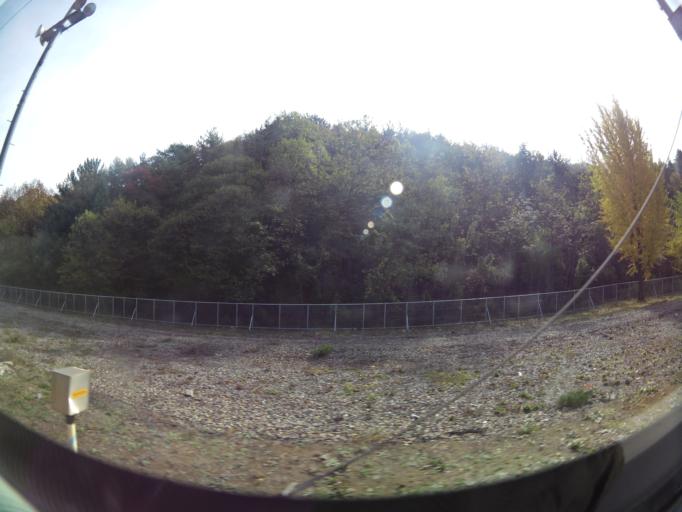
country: KR
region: Daejeon
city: Daejeon
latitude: 36.3373
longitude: 127.4921
